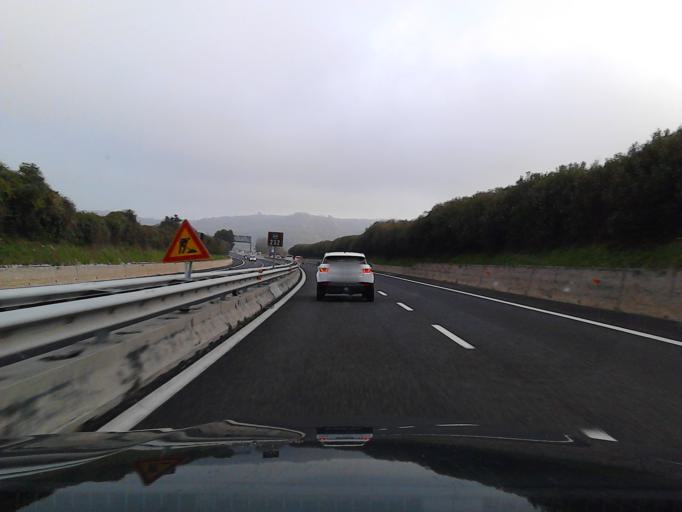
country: IT
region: Abruzzo
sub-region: Provincia di Chieti
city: Miglianico
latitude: 42.3786
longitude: 14.2948
